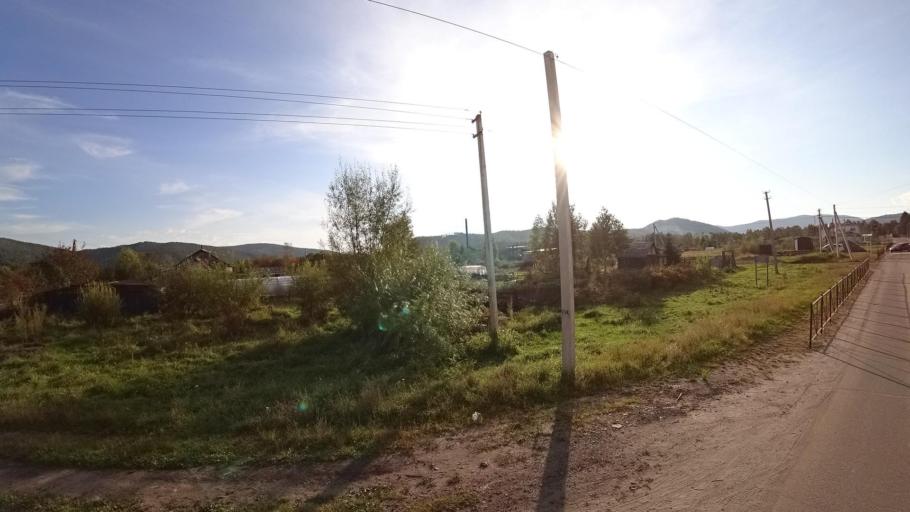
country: RU
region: Jewish Autonomous Oblast
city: Kul'dur
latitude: 49.2012
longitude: 131.6263
